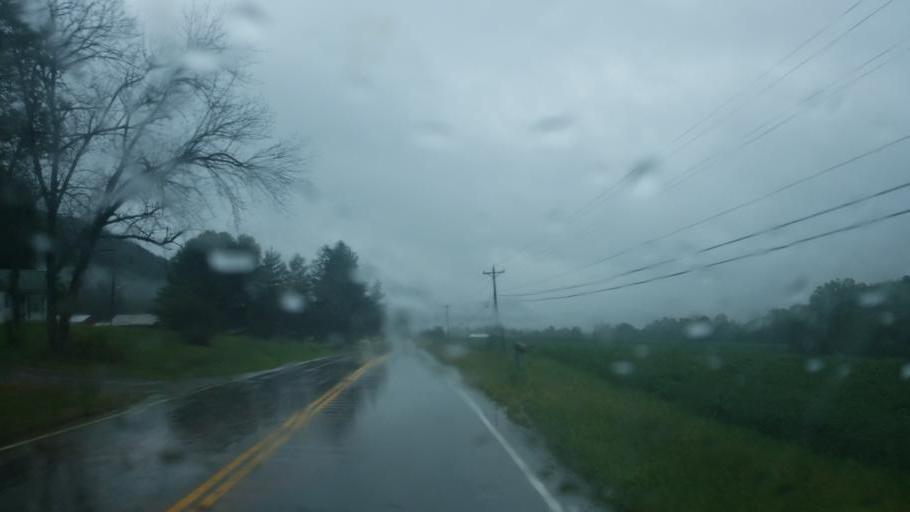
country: US
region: Kentucky
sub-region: Fleming County
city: Flemingsburg
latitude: 38.3251
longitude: -83.5850
